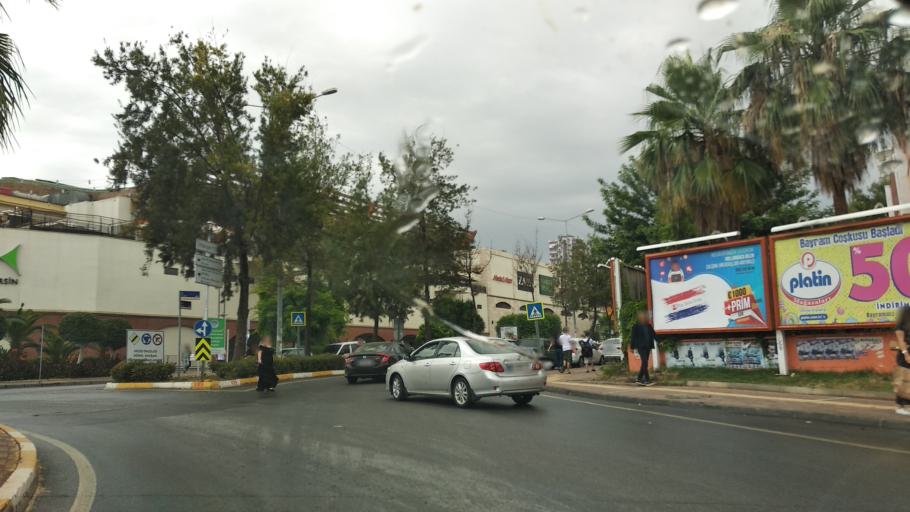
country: TR
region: Mersin
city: Mercin
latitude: 36.7849
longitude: 34.5896
